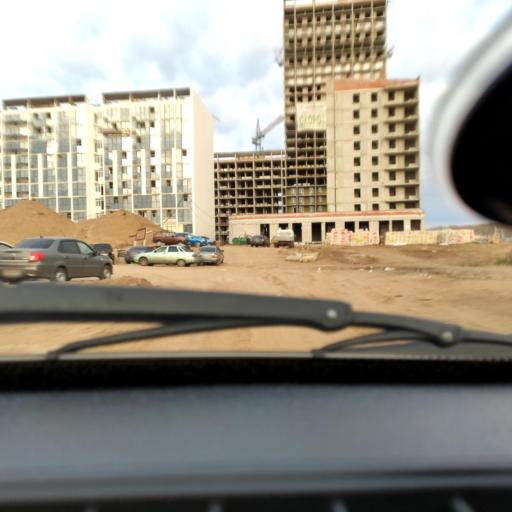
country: RU
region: Bashkortostan
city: Mikhaylovka
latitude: 54.7702
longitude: 55.9046
